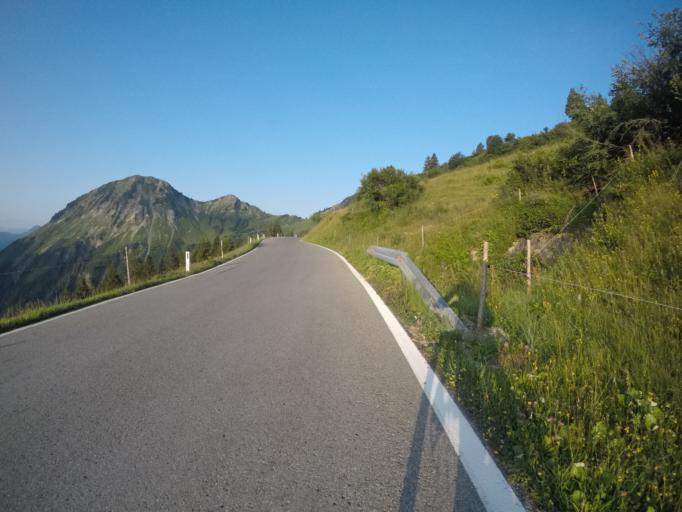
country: AT
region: Vorarlberg
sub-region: Politischer Bezirk Bregenz
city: Damuels
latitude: 47.2767
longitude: 9.8459
